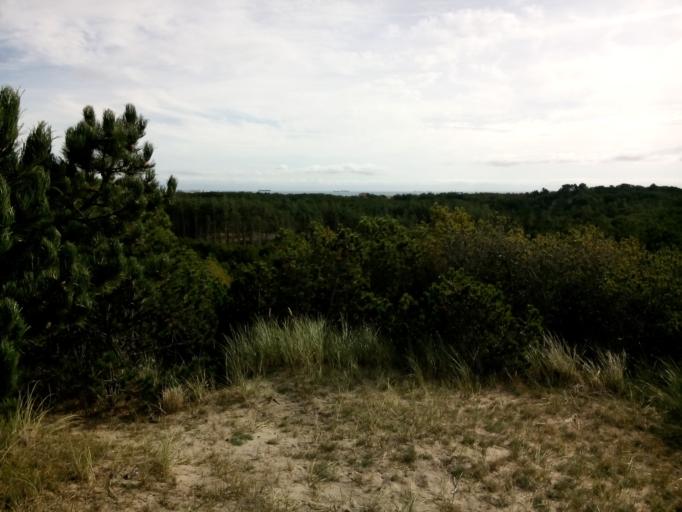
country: DK
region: North Denmark
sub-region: Frederikshavn Kommune
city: Skagen
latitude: 57.7187
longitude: 10.5450
